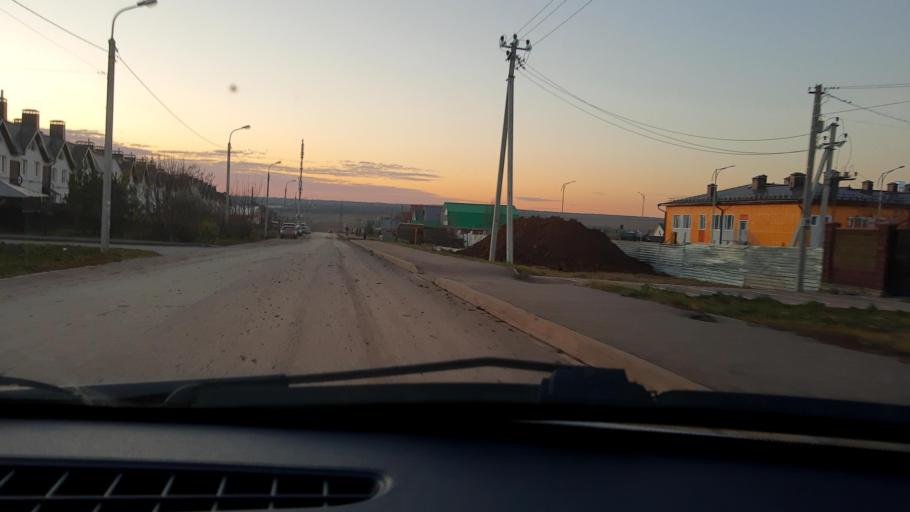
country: RU
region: Bashkortostan
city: Avdon
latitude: 54.6977
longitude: 55.8006
